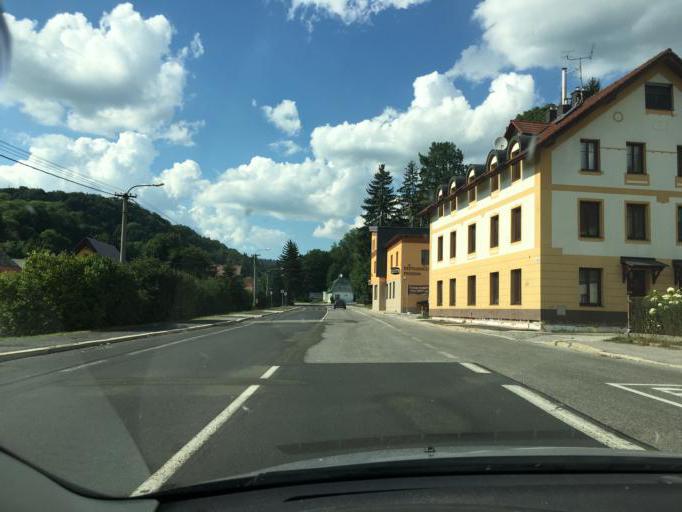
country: CZ
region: Kralovehradecky
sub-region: Okres Trutnov
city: Vrchlabi
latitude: 50.6458
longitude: 15.6079
